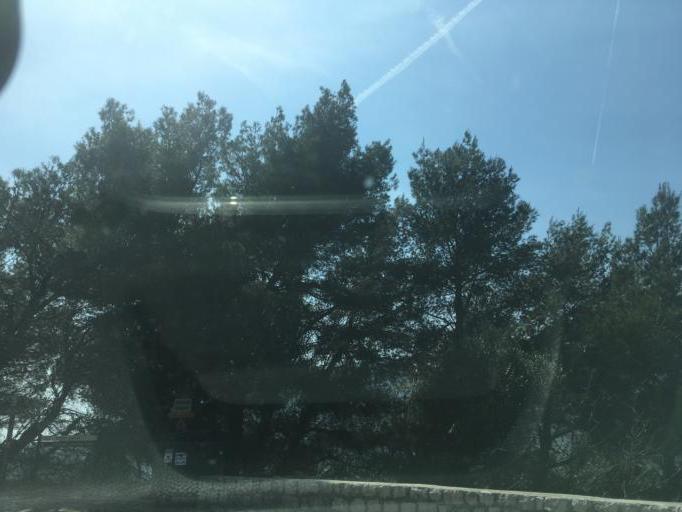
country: FR
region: Provence-Alpes-Cote d'Azur
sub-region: Departement des Alpes-Maritimes
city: Saint-Martin-du-Var
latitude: 43.8272
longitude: 7.1954
